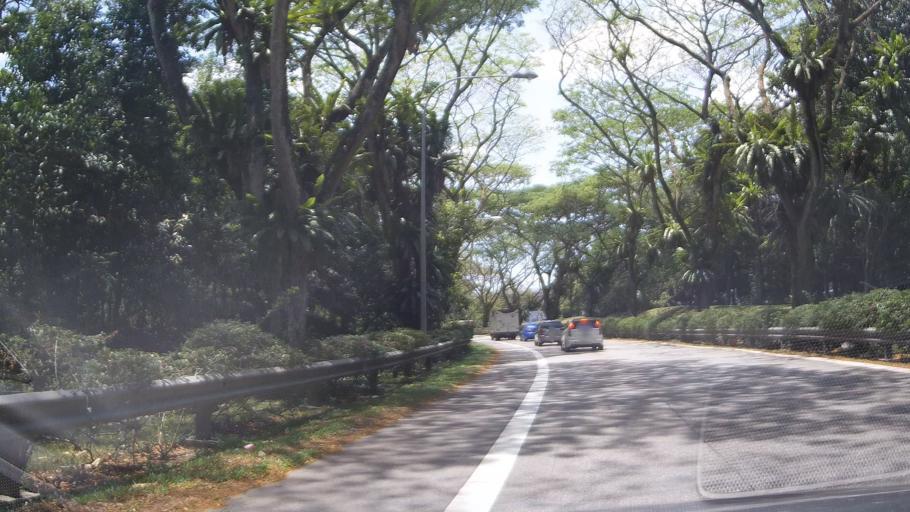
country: MY
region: Johor
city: Johor Bahru
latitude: 1.3639
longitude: 103.7085
